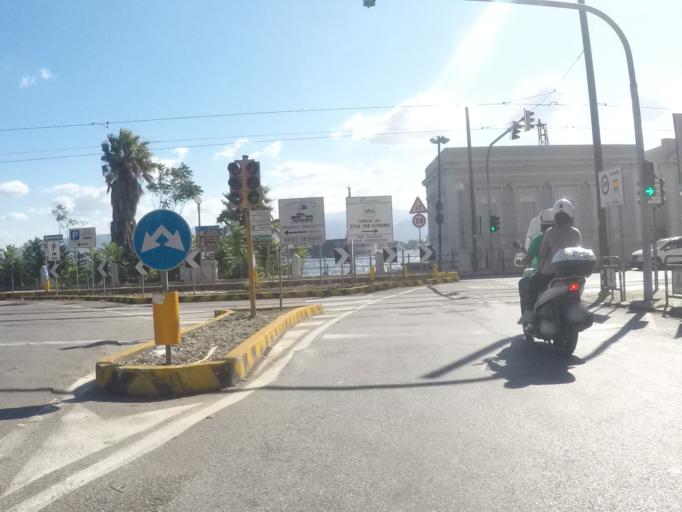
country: IT
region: Sicily
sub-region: Messina
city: Messina
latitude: 38.1971
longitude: 15.5576
